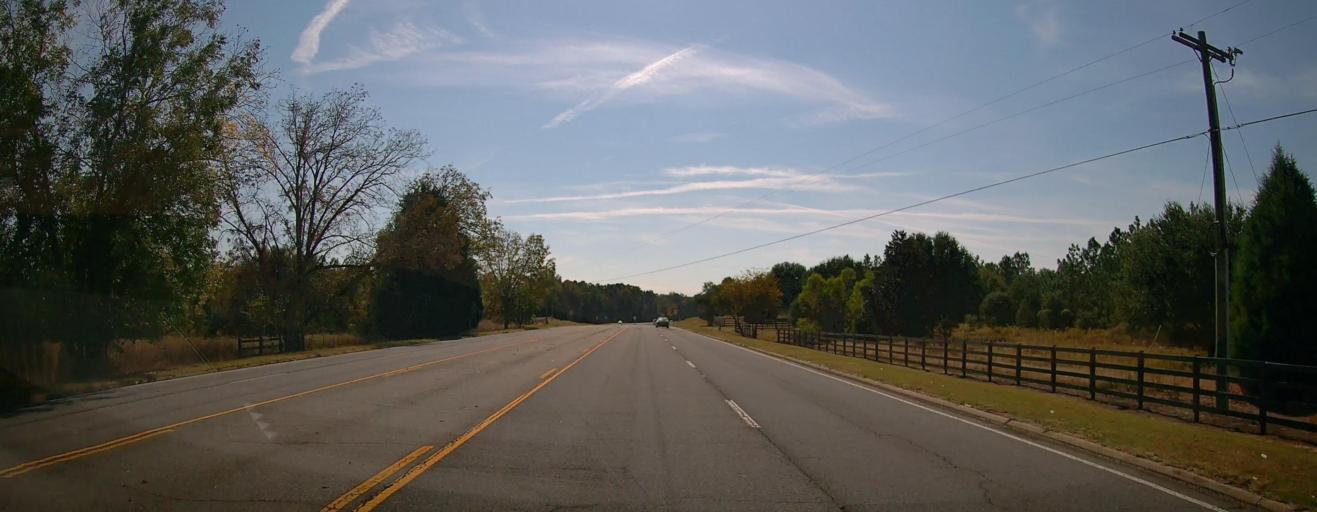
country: US
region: Georgia
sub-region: Lee County
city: Leesburg
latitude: 31.7647
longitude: -83.9743
